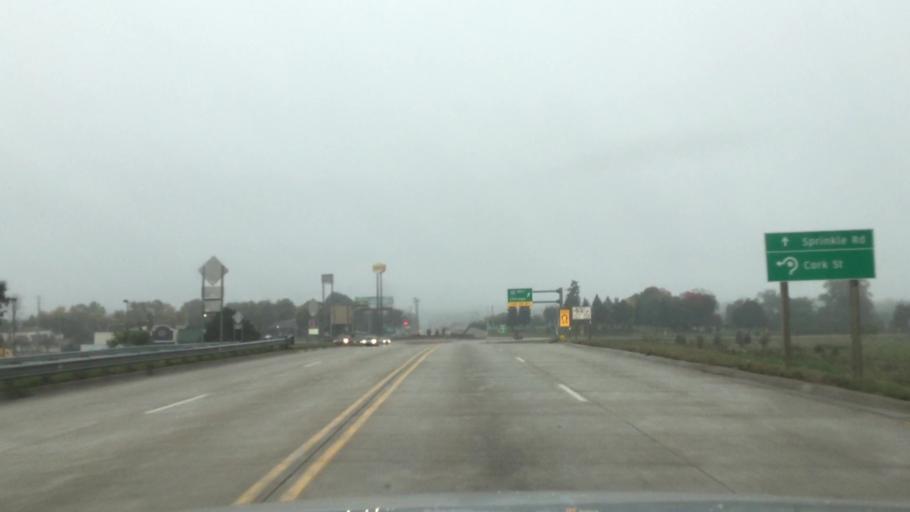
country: US
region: Michigan
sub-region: Kalamazoo County
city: Eastwood
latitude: 42.2599
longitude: -85.5311
